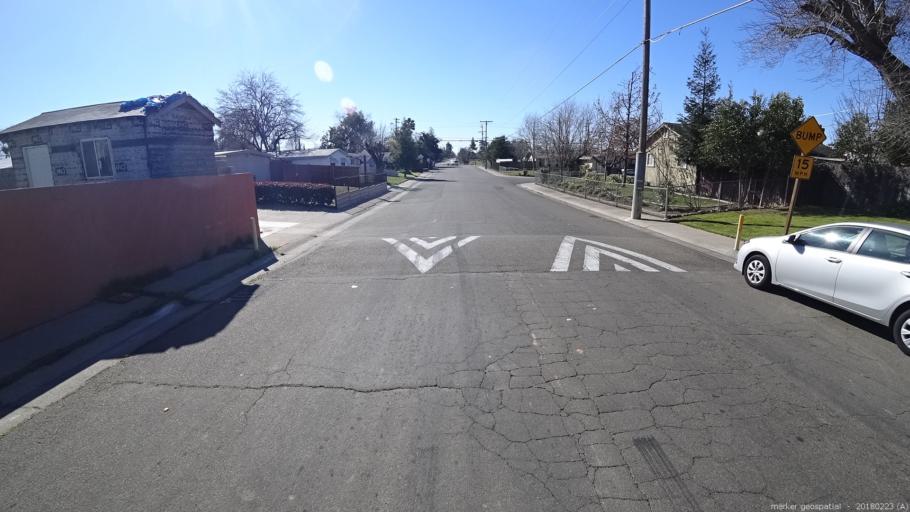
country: US
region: California
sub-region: Sacramento County
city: North Highlands
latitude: 38.7055
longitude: -121.3921
